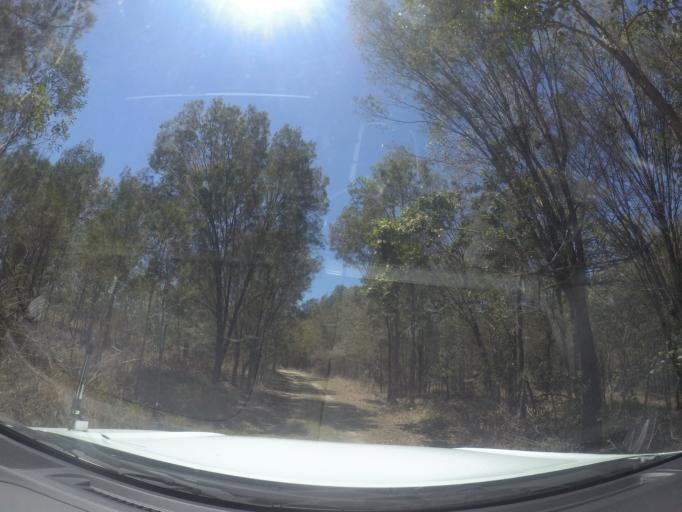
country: AU
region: Queensland
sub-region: Logan
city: Logan Reserve
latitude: -27.7435
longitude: 153.1287
